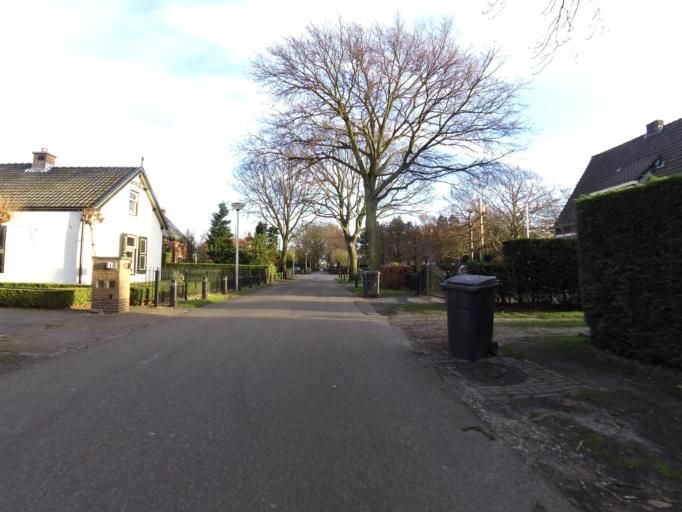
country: NL
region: South Holland
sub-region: Gemeente Brielle
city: Brielle
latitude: 51.9073
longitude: 4.0929
